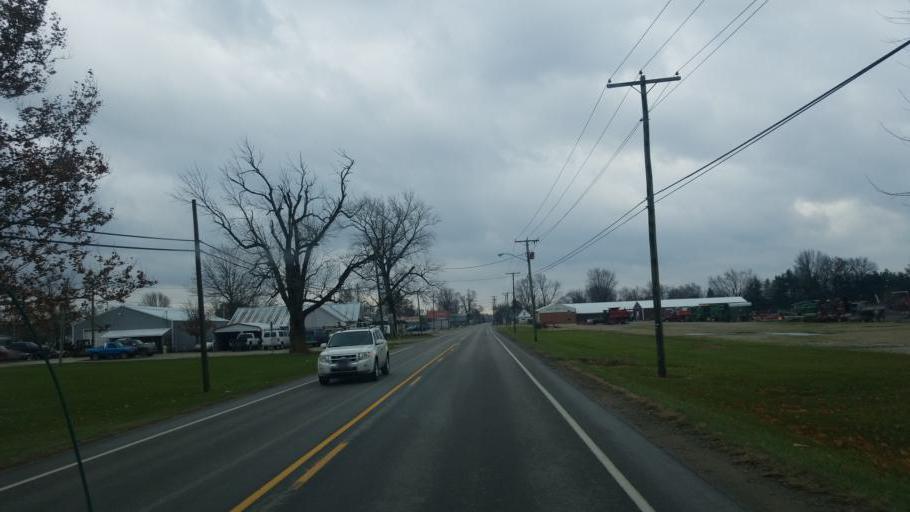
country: US
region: Indiana
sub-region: Adams County
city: Geneva
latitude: 40.5385
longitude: -84.9647
